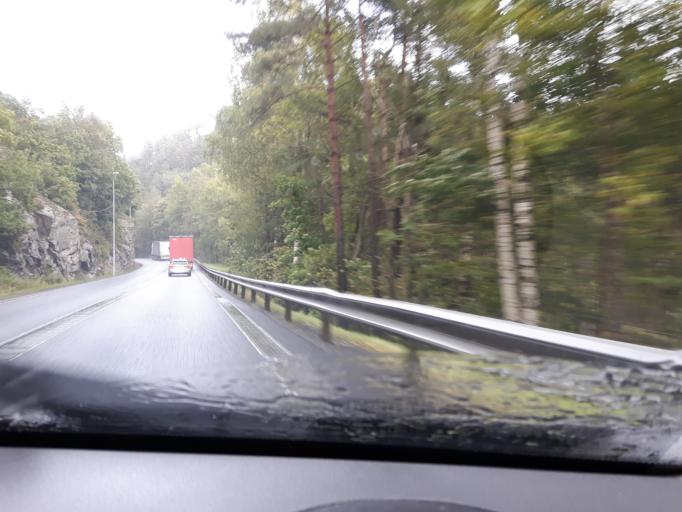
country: NO
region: Vest-Agder
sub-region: Sogne
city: Sogne
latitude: 58.0941
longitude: 7.6924
